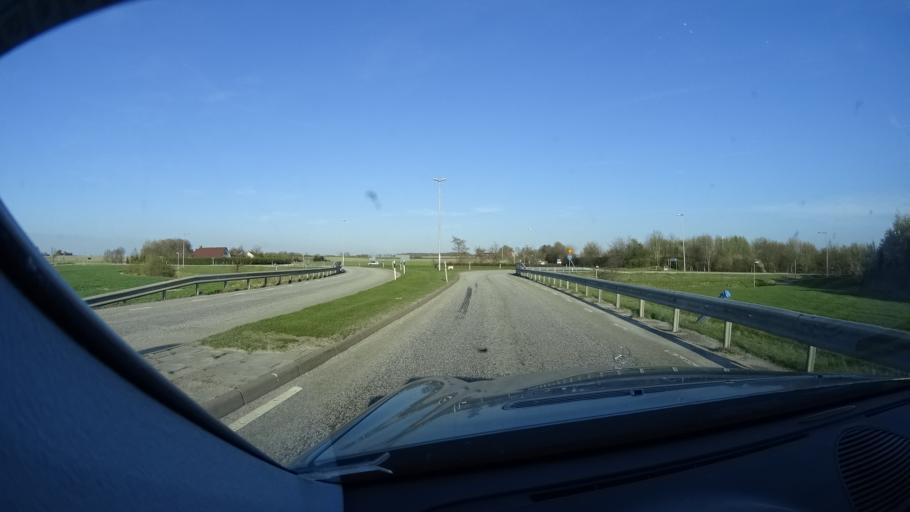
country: SE
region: Skane
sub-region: Eslovs Kommun
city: Eslov
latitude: 55.8557
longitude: 13.3039
